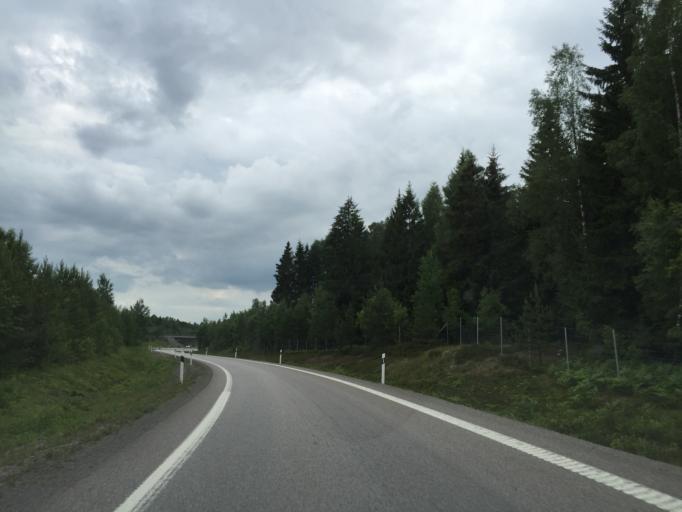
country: SE
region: OErebro
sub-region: Lindesbergs Kommun
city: Fellingsbro
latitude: 59.3393
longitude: 15.5365
